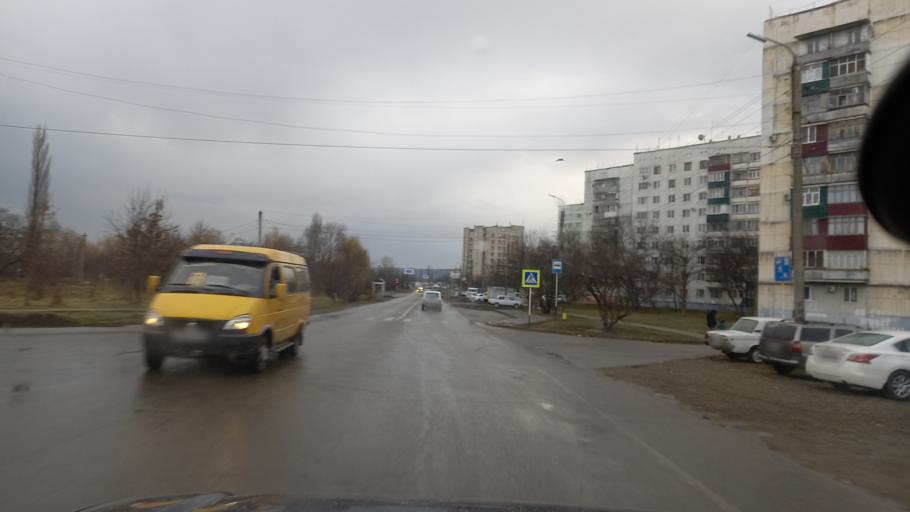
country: RU
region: Adygeya
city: Maykop
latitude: 44.5783
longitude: 40.1354
